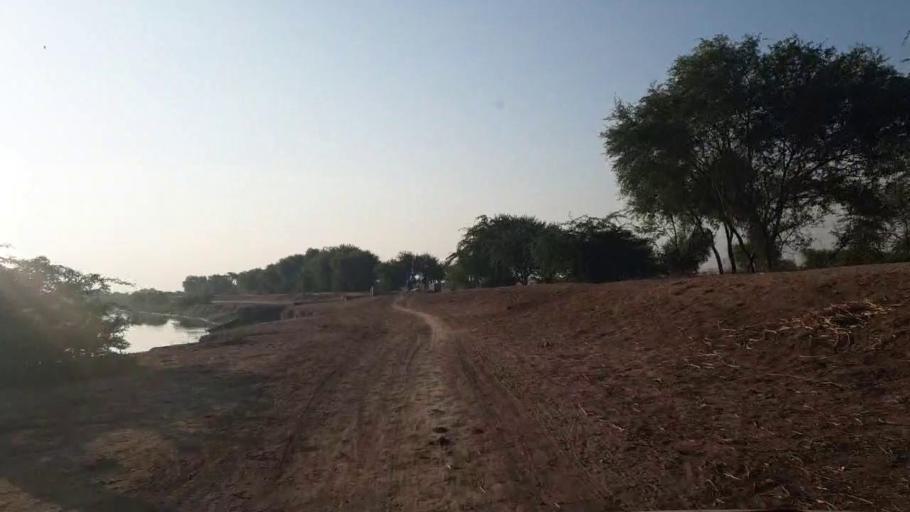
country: PK
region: Sindh
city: Badin
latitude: 24.6378
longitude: 68.7920
